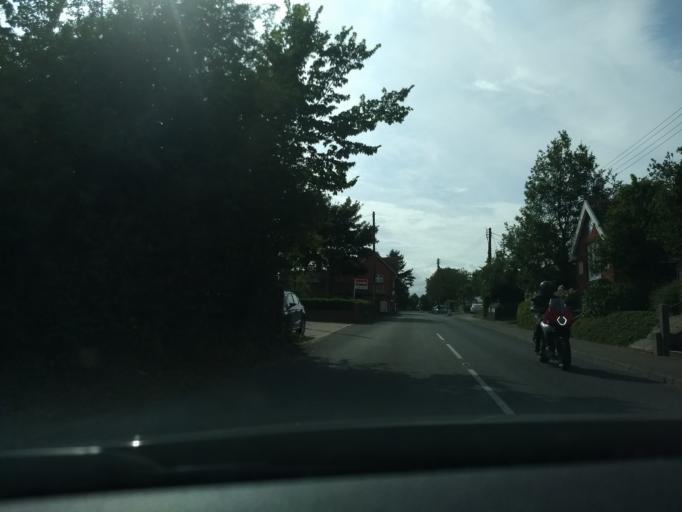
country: GB
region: England
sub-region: Suffolk
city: Shotley Gate
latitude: 51.9893
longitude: 1.2084
